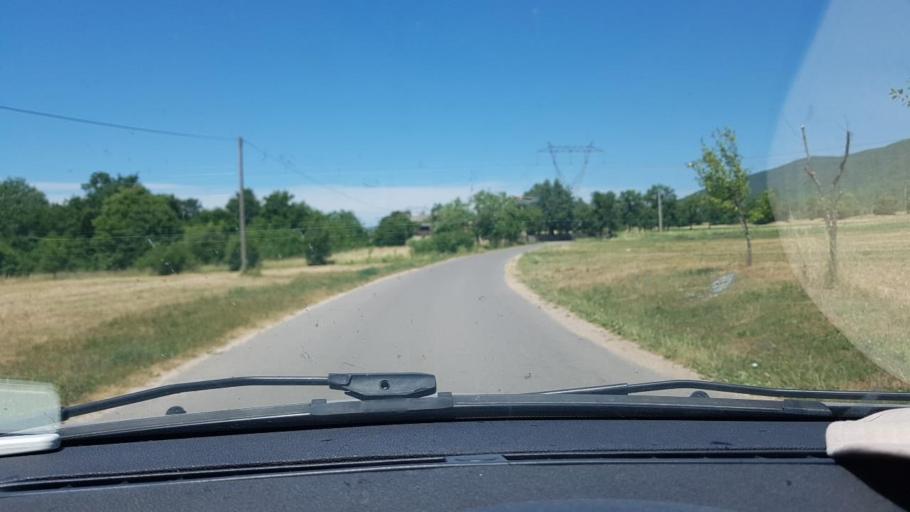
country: HR
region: Licko-Senjska
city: Otocac
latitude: 44.7937
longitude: 15.3660
